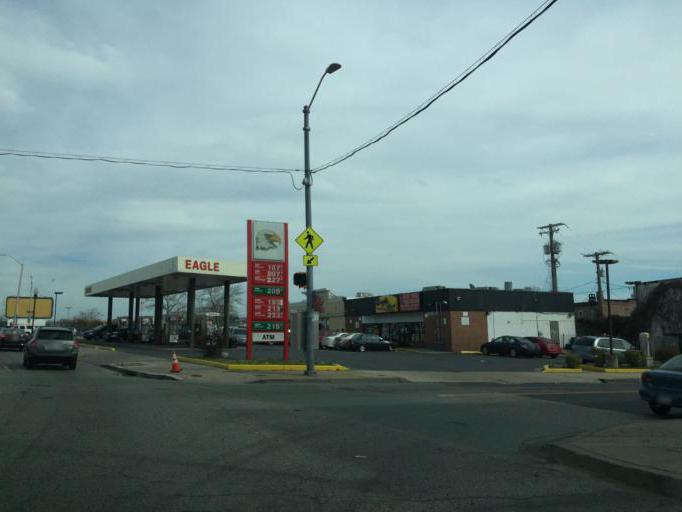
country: US
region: Maryland
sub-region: City of Baltimore
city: Baltimore
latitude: 39.2955
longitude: -76.5737
